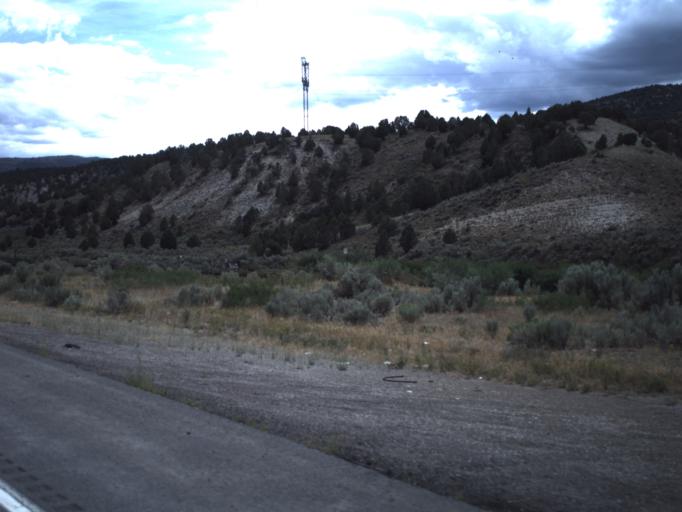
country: US
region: Utah
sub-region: Utah County
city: Mapleton
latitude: 39.9815
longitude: -111.3561
